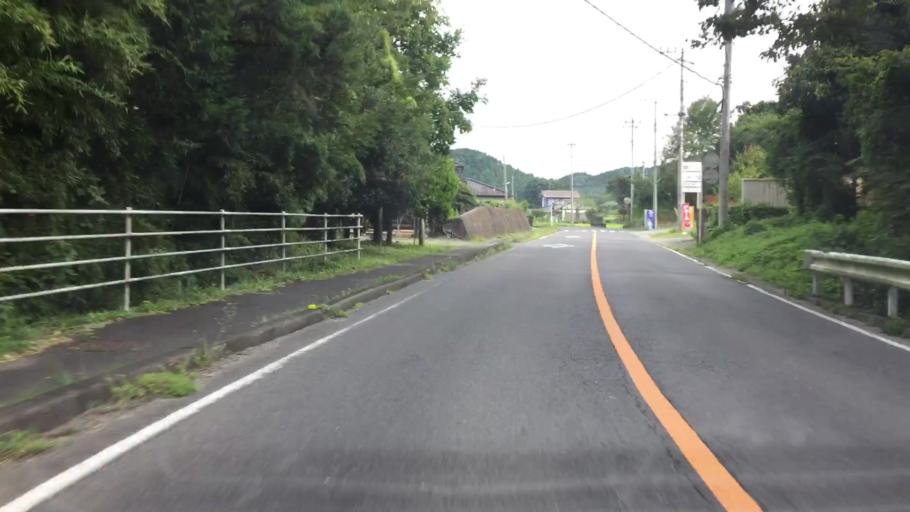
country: JP
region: Tochigi
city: Imaichi
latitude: 36.7473
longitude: 139.7369
